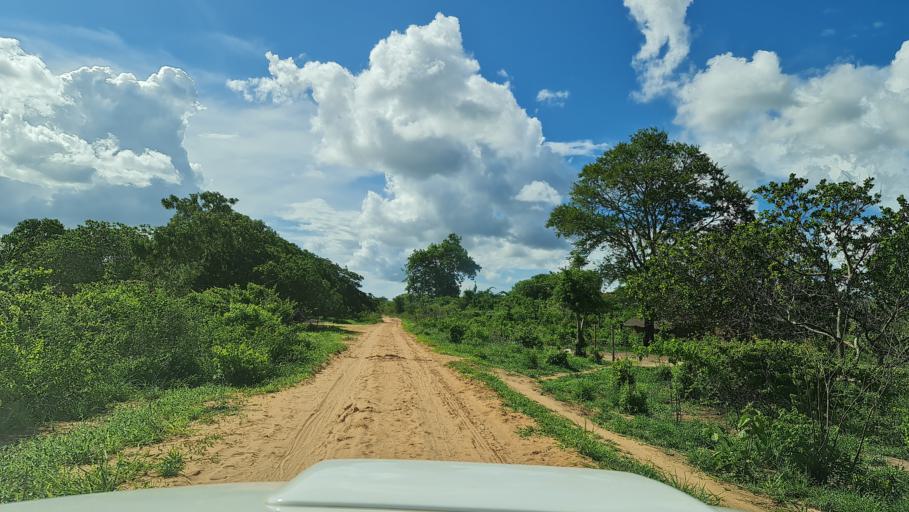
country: MZ
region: Nampula
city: Ilha de Mocambique
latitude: -15.4155
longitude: 40.2584
